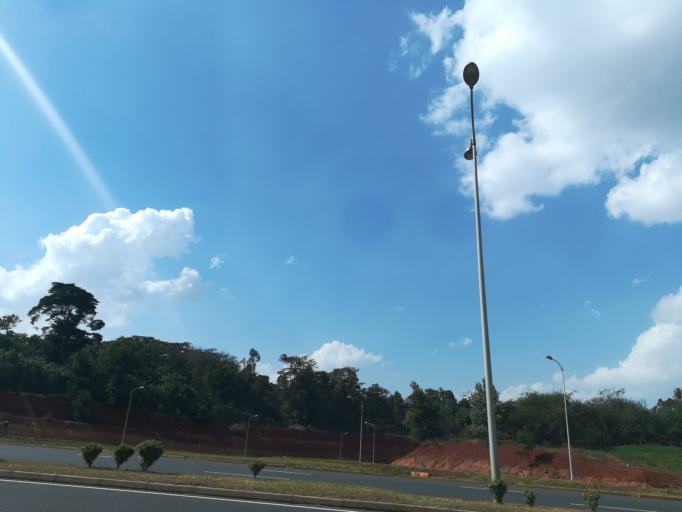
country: KE
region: Kajiado
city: Ngong
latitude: -1.3085
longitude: 36.7263
